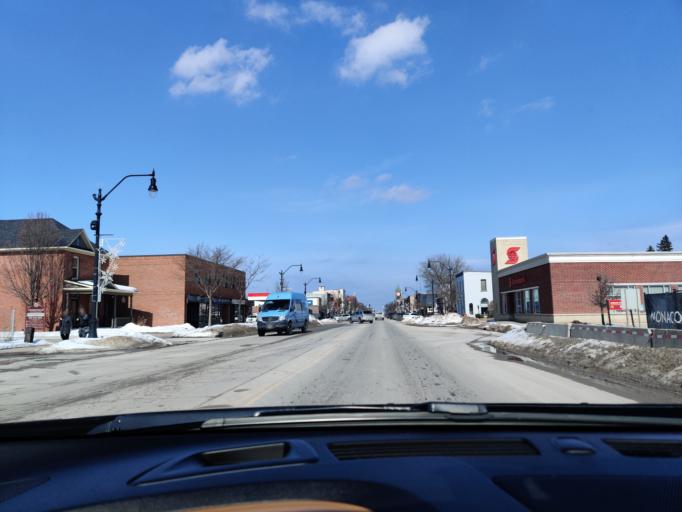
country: CA
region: Ontario
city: Collingwood
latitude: 44.4962
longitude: -80.2161
